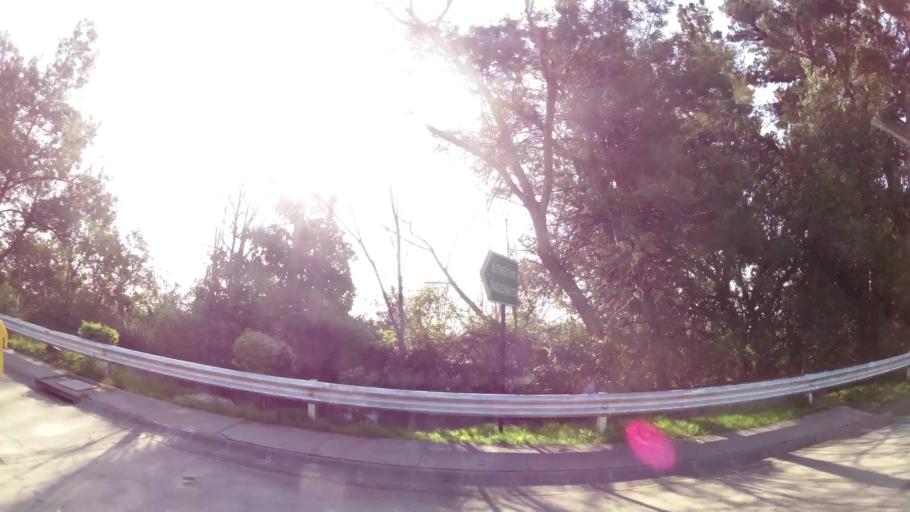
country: CL
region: Santiago Metropolitan
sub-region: Provincia de Santiago
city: Villa Presidente Frei, Nunoa, Santiago, Chile
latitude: -33.3773
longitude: -70.5008
